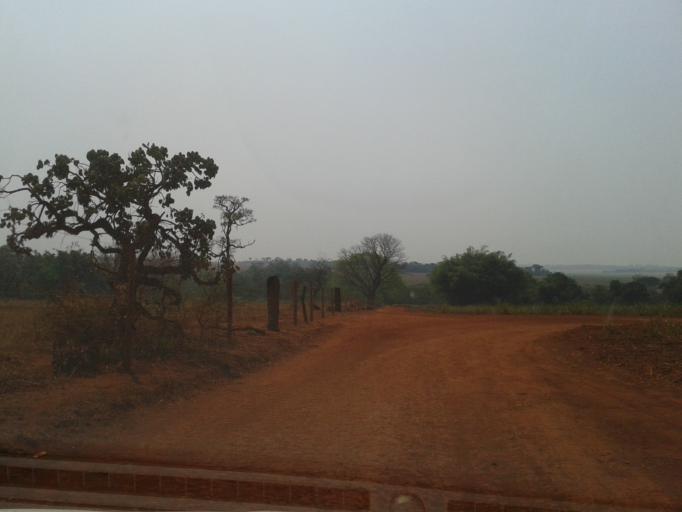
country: BR
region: Minas Gerais
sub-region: Centralina
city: Centralina
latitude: -18.6356
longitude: -49.2493
